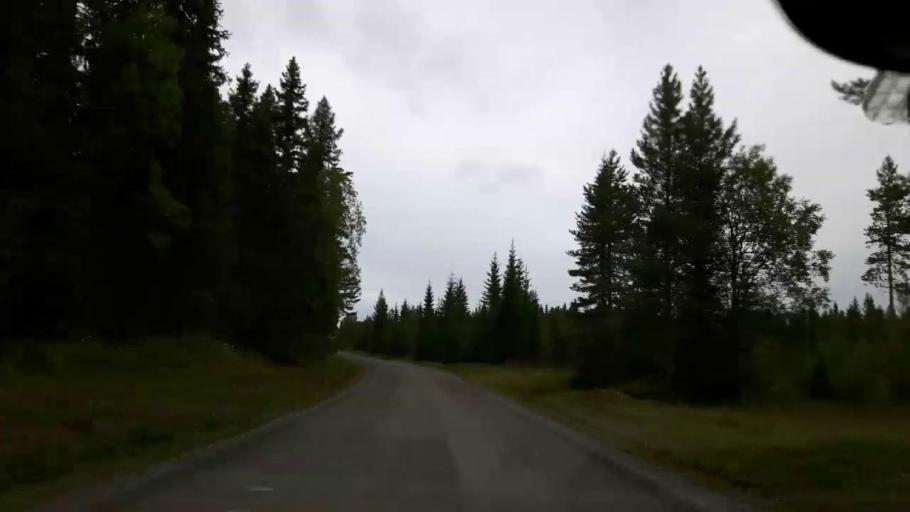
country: SE
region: Jaemtland
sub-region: OEstersunds Kommun
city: Ostersund
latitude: 63.1245
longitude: 14.5368
